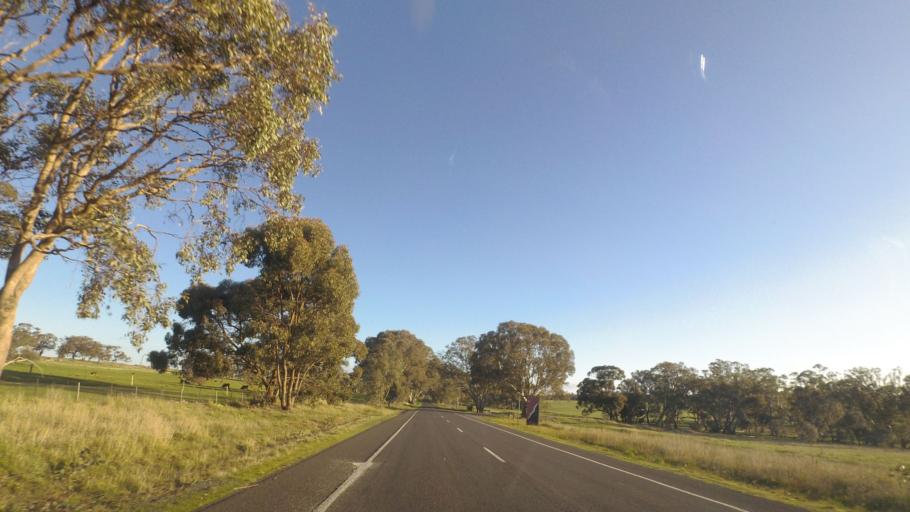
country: AU
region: Victoria
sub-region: Mount Alexander
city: Castlemaine
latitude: -37.0536
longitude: 144.5248
